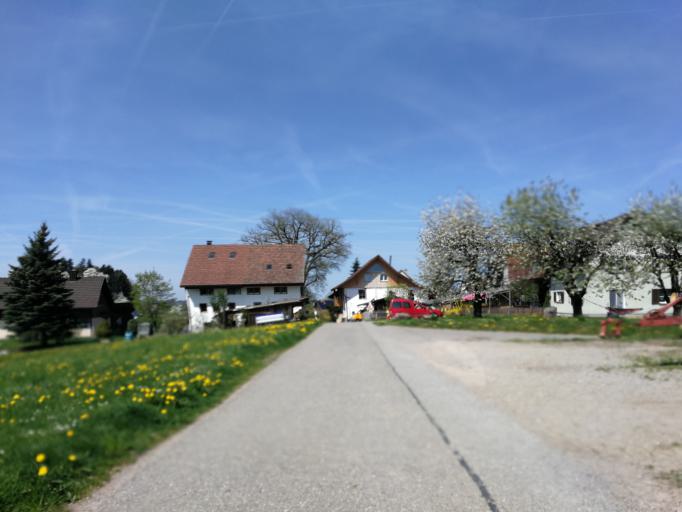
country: CH
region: Zurich
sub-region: Bezirk Hinwil
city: Wetzikon / Unter-Wetzikon
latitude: 47.3067
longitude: 8.8142
